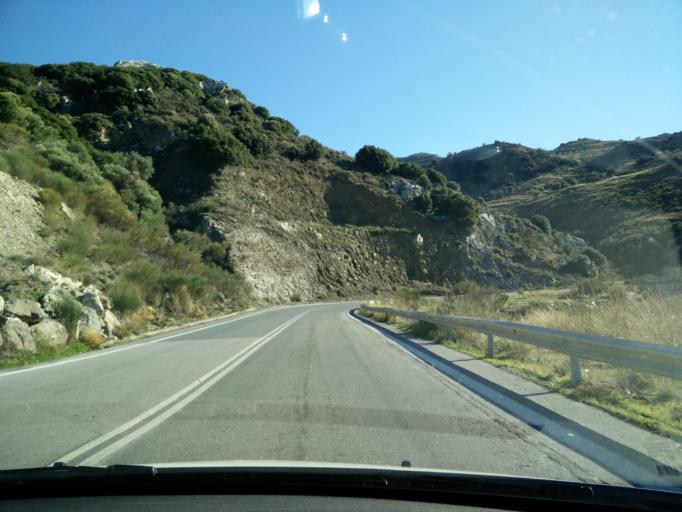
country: GR
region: Crete
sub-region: Nomos Irakleiou
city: Arkalochori
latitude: 35.0696
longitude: 25.3615
